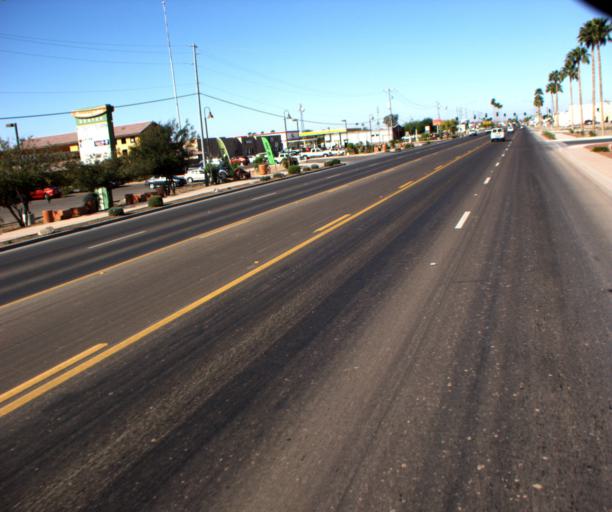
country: US
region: Arizona
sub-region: Yuma County
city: Somerton
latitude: 32.5968
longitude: -114.7019
